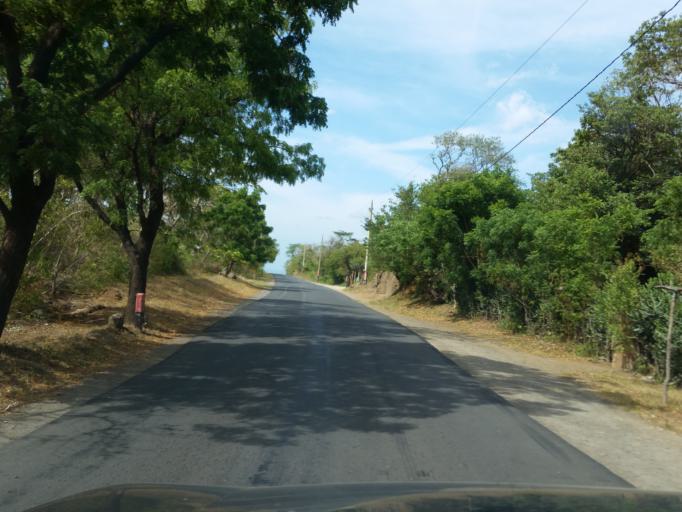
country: NI
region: Managua
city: San Rafael del Sur
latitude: 11.9077
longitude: -86.3831
